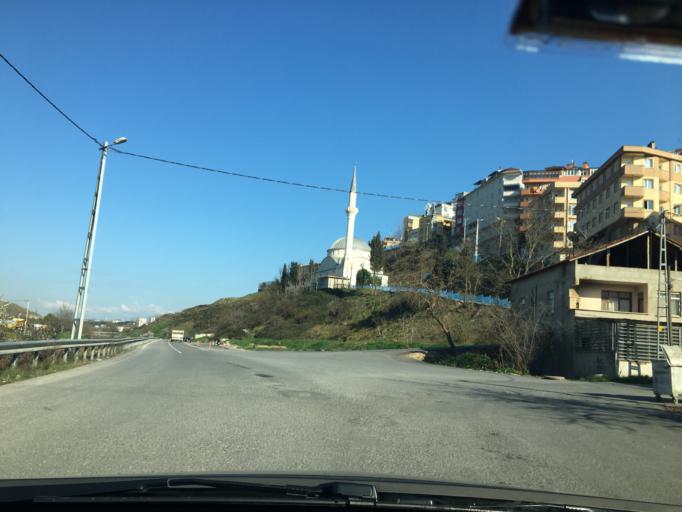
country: TR
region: Istanbul
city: Pendik
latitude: 40.8716
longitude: 29.2903
